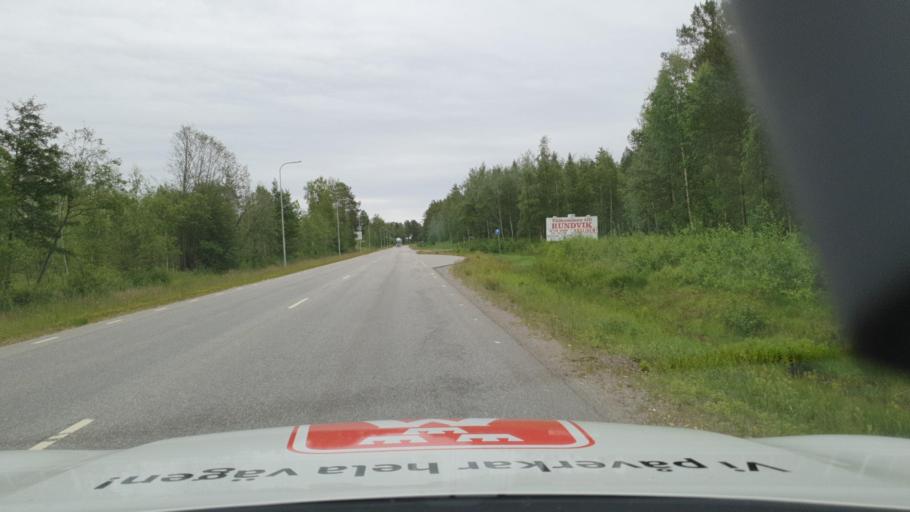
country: SE
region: Vaesterbotten
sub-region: Nordmalings Kommun
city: Nordmaling
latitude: 63.5479
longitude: 19.4253
